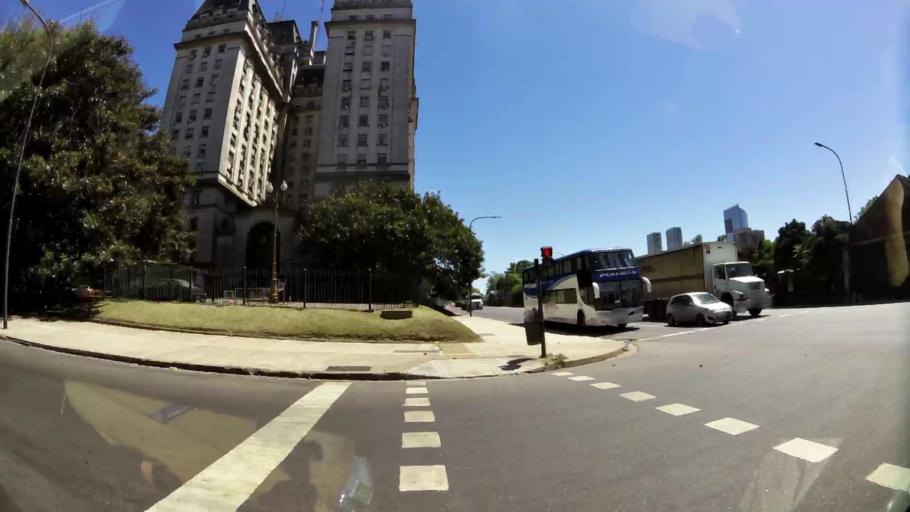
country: AR
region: Buenos Aires F.D.
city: Buenos Aires
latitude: -34.6110
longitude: -58.3674
